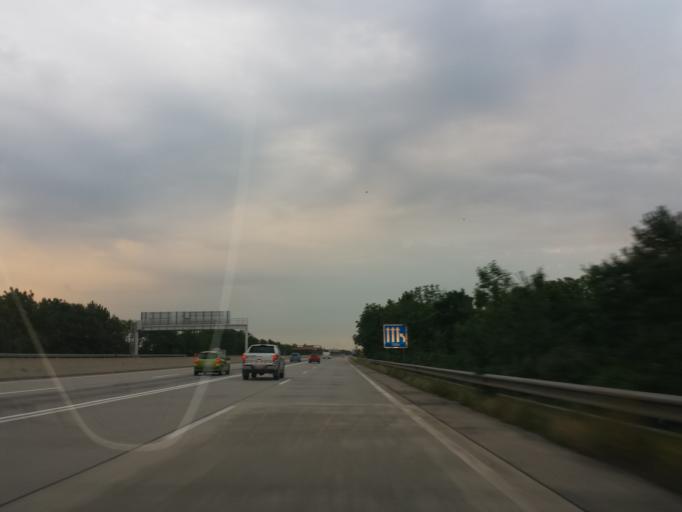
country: AT
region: Lower Austria
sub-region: Politischer Bezirk Neunkirchen
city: Breitenau
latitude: 47.7229
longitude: 16.1420
